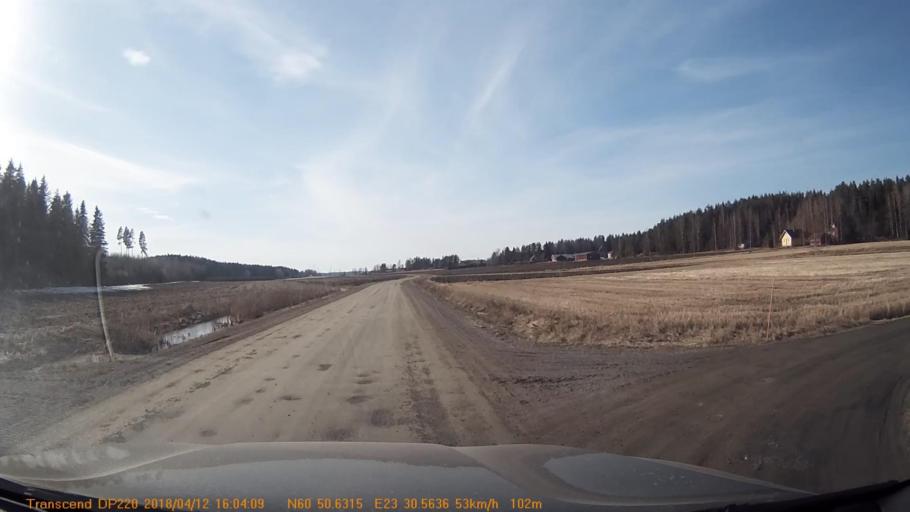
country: FI
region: Haeme
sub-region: Forssa
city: Jokioinen
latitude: 60.8439
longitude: 23.5091
